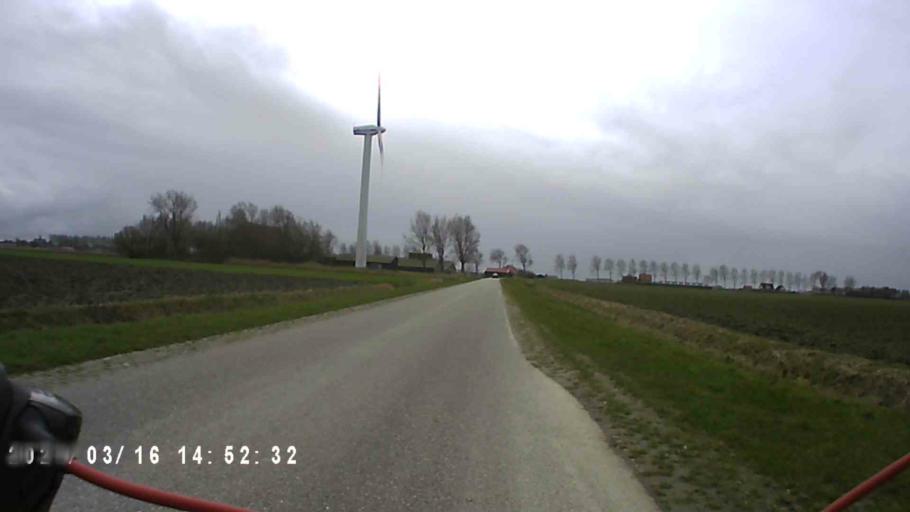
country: NL
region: Friesland
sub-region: Gemeente Harlingen
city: Harlingen
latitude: 53.1126
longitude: 5.4623
